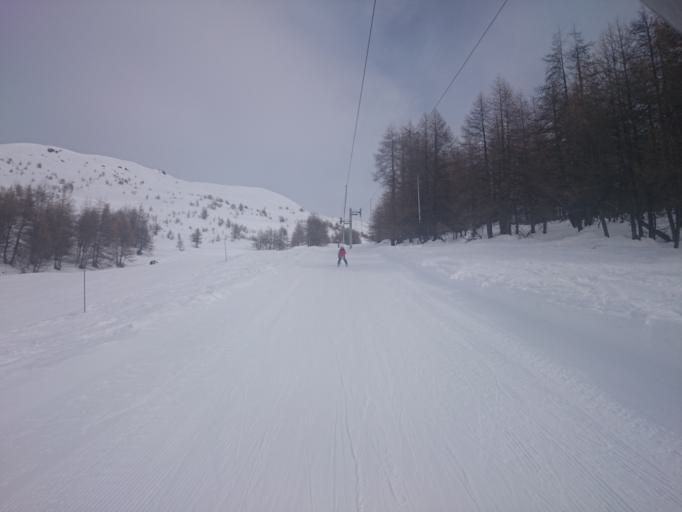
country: IT
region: Piedmont
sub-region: Provincia di Torino
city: Prali
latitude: 44.7915
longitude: 6.9553
